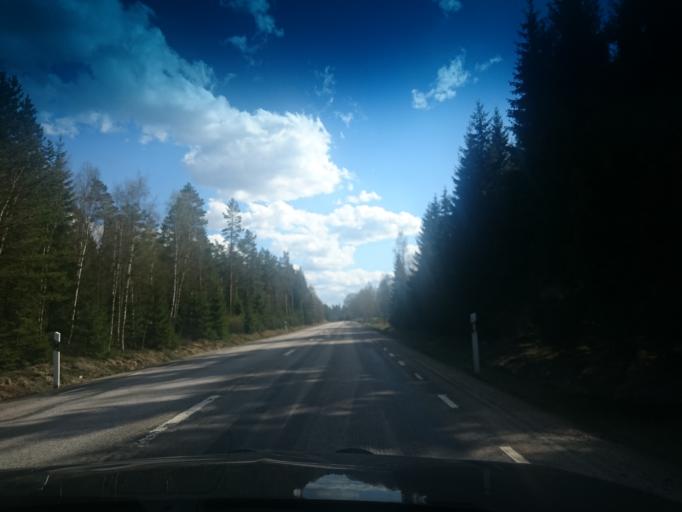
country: SE
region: Joenkoeping
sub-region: Vetlanda Kommun
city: Vetlanda
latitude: 57.2651
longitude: 15.1281
